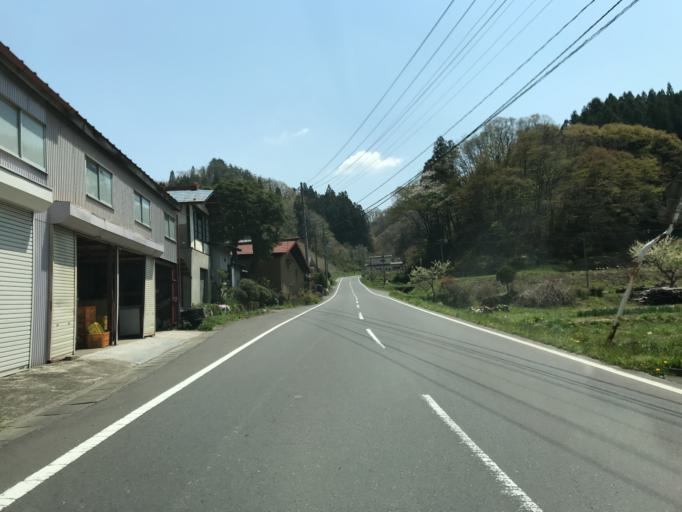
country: JP
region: Fukushima
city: Ishikawa
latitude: 37.0673
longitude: 140.4438
